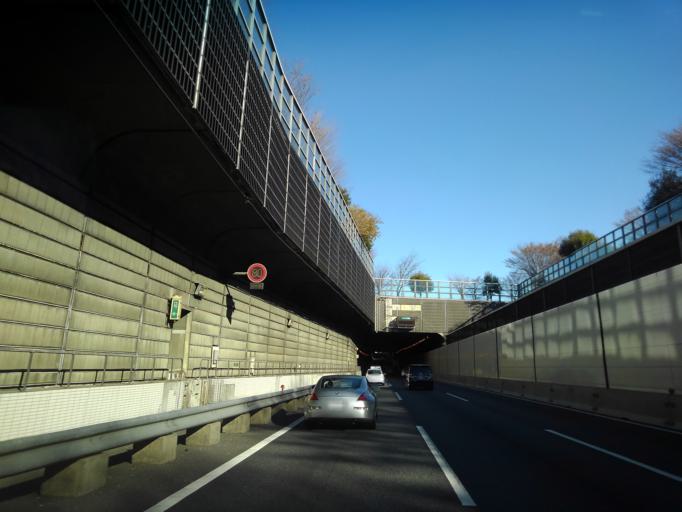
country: JP
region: Saitama
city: Wako
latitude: 35.7641
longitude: 139.5996
